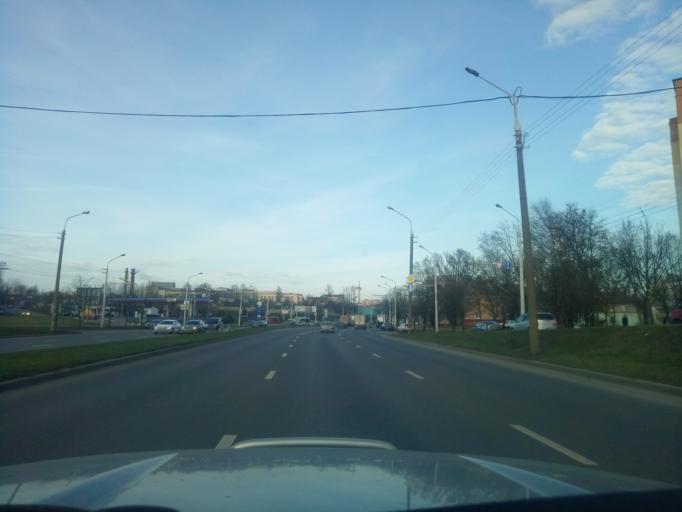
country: BY
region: Minsk
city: Novoye Medvezhino
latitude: 53.8848
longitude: 27.5037
